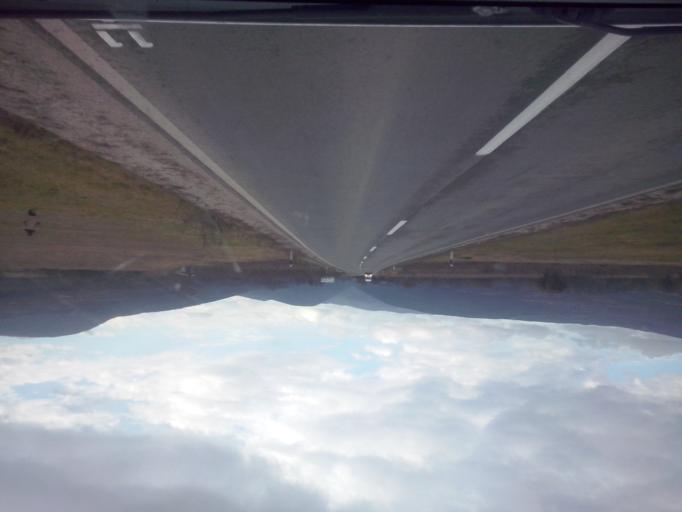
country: RS
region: Central Serbia
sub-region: Pomoravski Okrug
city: Paracin
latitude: 43.8550
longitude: 21.5627
